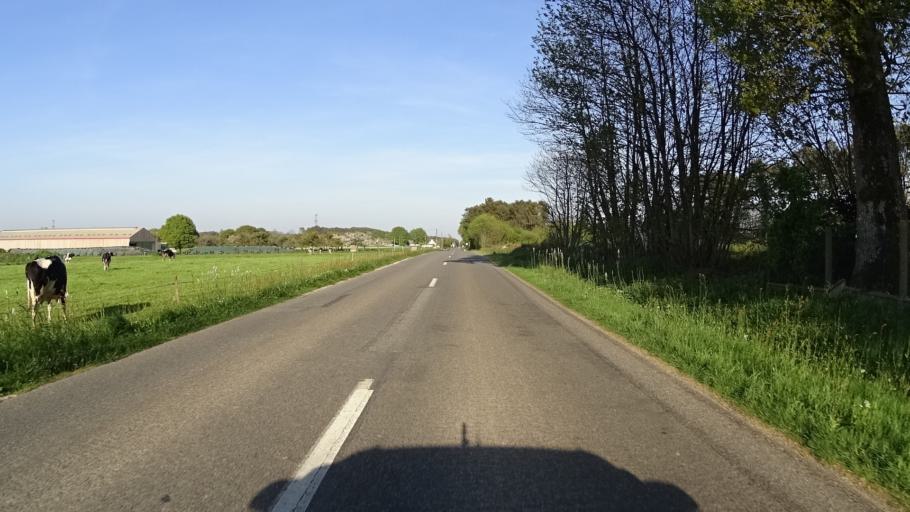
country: FR
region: Brittany
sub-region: Departement du Morbihan
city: Allaire
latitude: 47.6111
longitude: -2.1827
